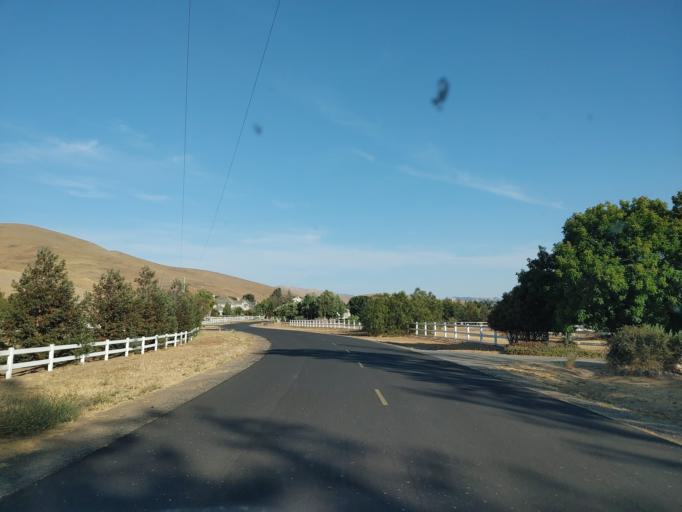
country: US
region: California
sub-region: San Benito County
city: Ridgemark
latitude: 36.7999
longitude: -121.3273
